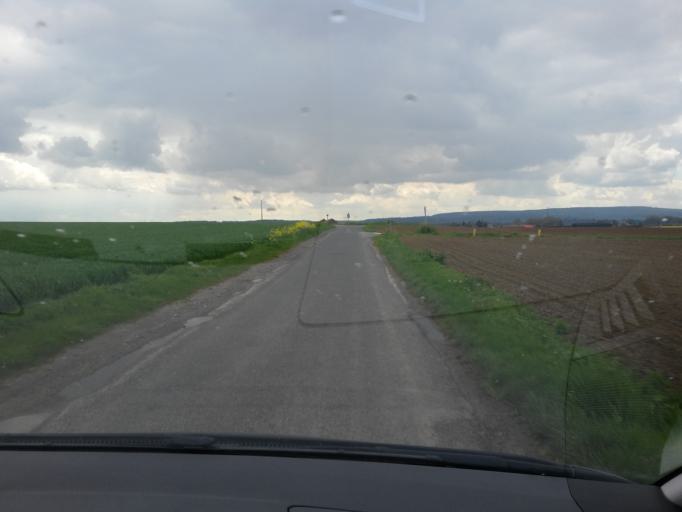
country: FR
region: Picardie
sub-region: Departement de l'Oise
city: Chevrieres
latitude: 49.3603
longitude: 2.6844
